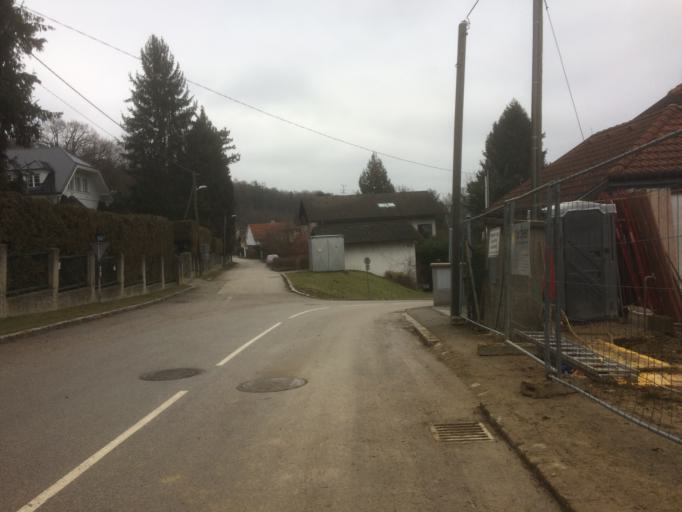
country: AT
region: Lower Austria
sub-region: Politischer Bezirk Wien-Umgebung
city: Gablitz
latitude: 48.2238
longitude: 16.1308
